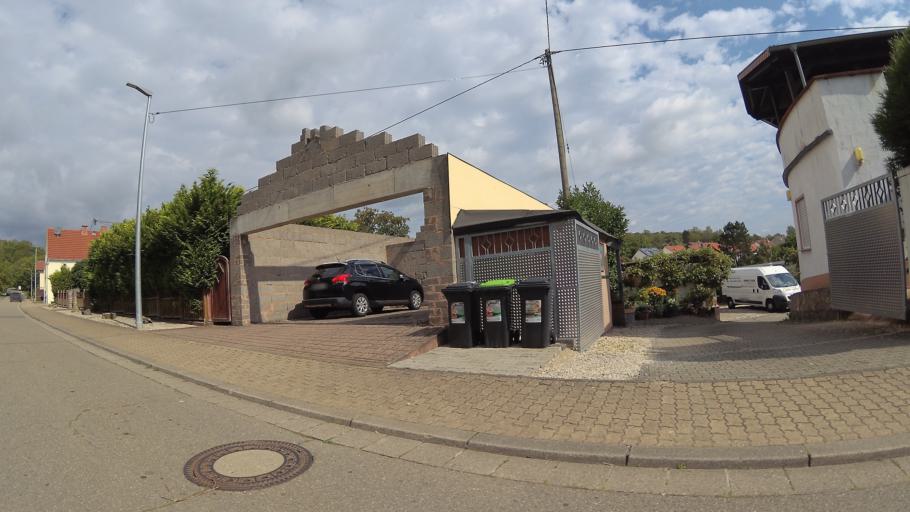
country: FR
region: Lorraine
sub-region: Departement de la Moselle
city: Bliesbruck
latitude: 49.1392
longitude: 7.1776
